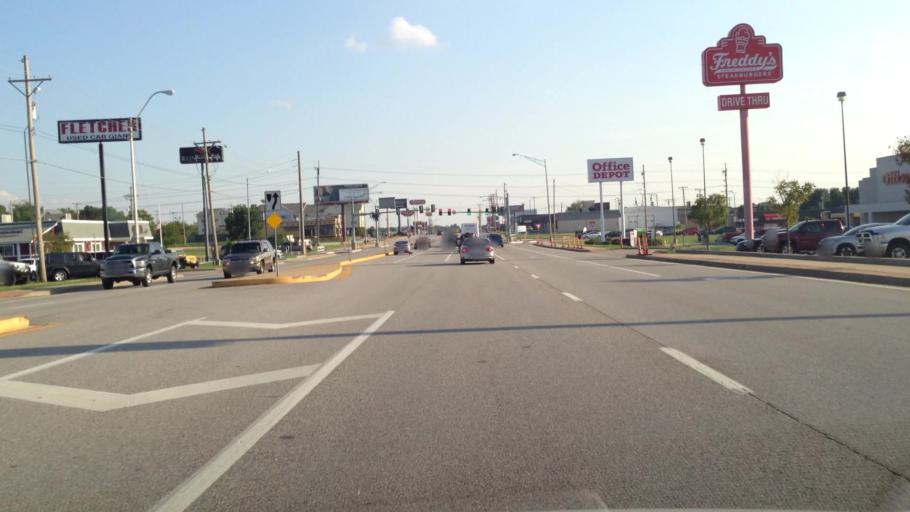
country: US
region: Missouri
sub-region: Jasper County
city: Duquesne
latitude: 37.0567
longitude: -94.4783
